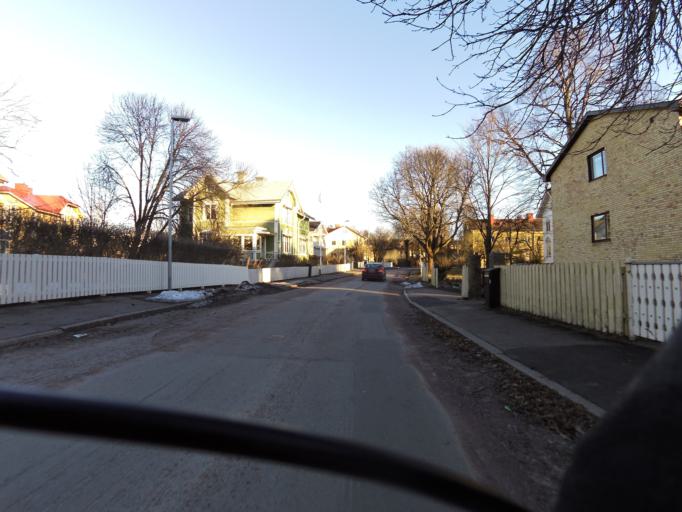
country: SE
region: Gaevleborg
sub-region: Gavle Kommun
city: Gavle
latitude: 60.6706
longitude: 17.1370
